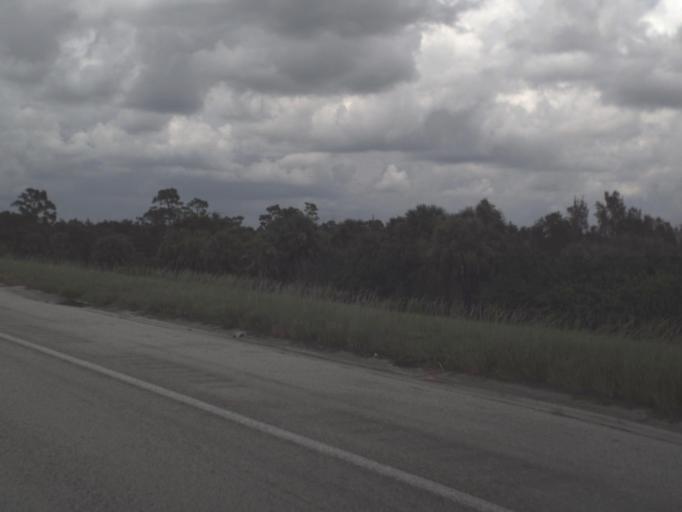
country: US
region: Florida
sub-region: Charlotte County
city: Harbour Heights
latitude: 26.9750
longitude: -82.0207
